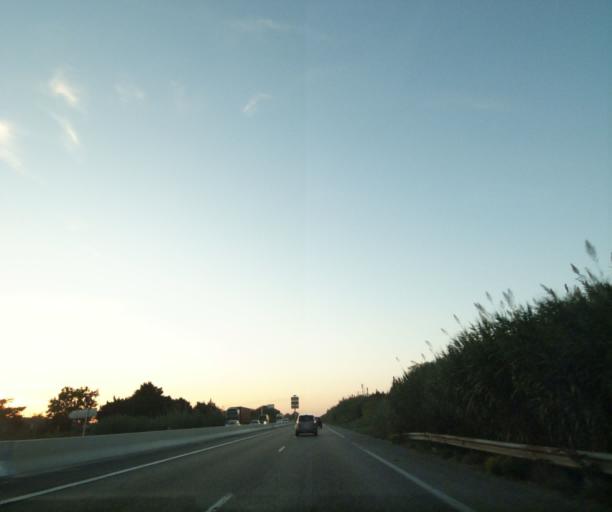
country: FR
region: Provence-Alpes-Cote d'Azur
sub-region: Departement des Bouches-du-Rhone
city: Fontvieille
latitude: 43.6424
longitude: 4.7117
